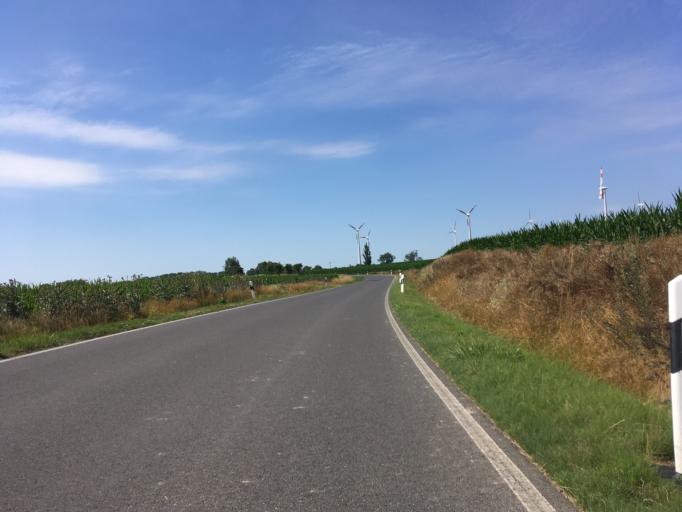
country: DE
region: Brandenburg
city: Gramzow
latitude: 53.2665
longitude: 14.0684
